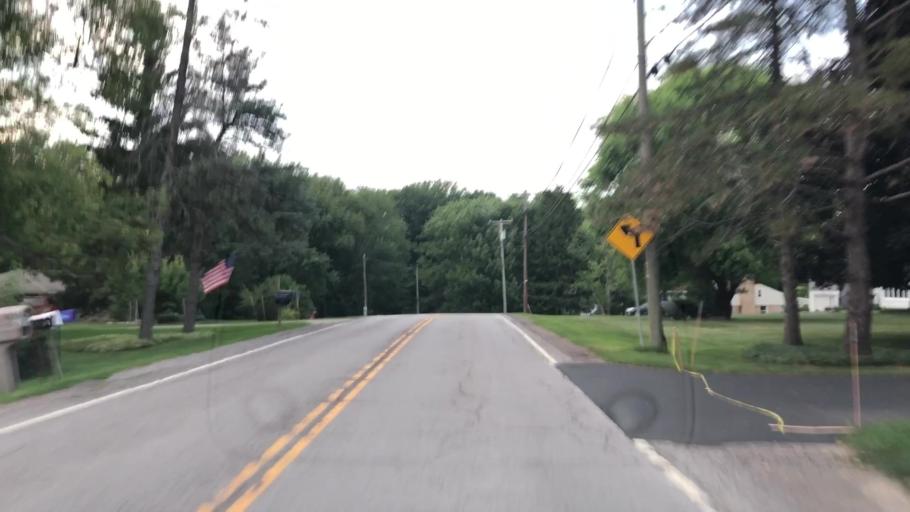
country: US
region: New York
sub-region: Erie County
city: East Aurora
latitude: 42.7802
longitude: -78.6032
